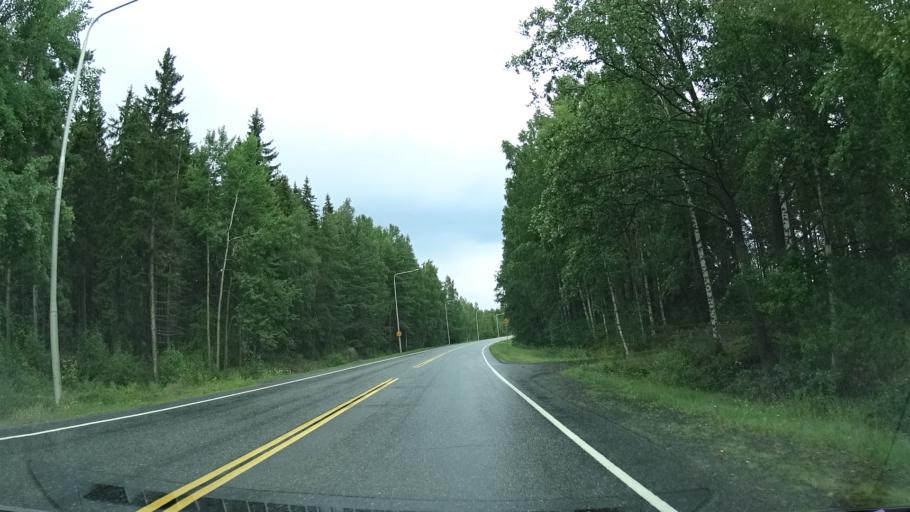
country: FI
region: Pirkanmaa
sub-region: Etelae-Pirkanmaa
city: Valkeakoski
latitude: 61.1806
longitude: 24.0387
